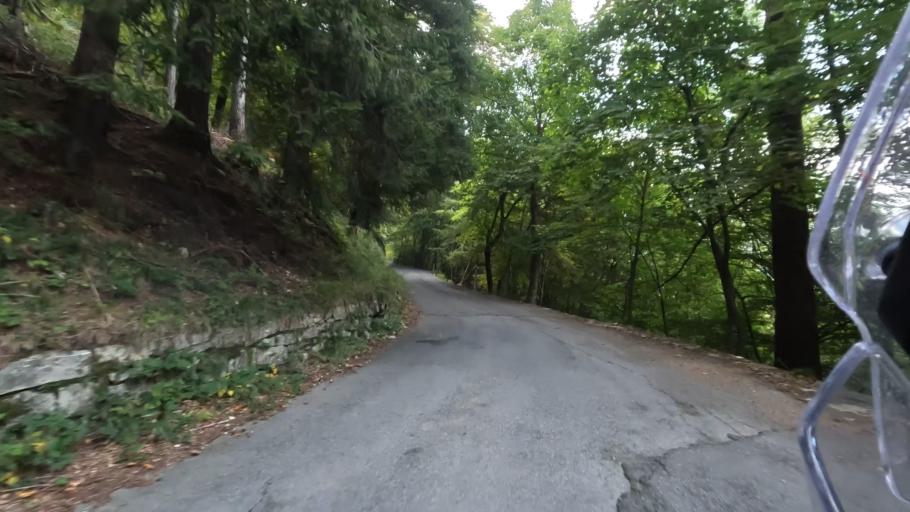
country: IT
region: Lombardy
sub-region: Provincia di Como
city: Pigra
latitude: 45.9615
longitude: 9.1258
